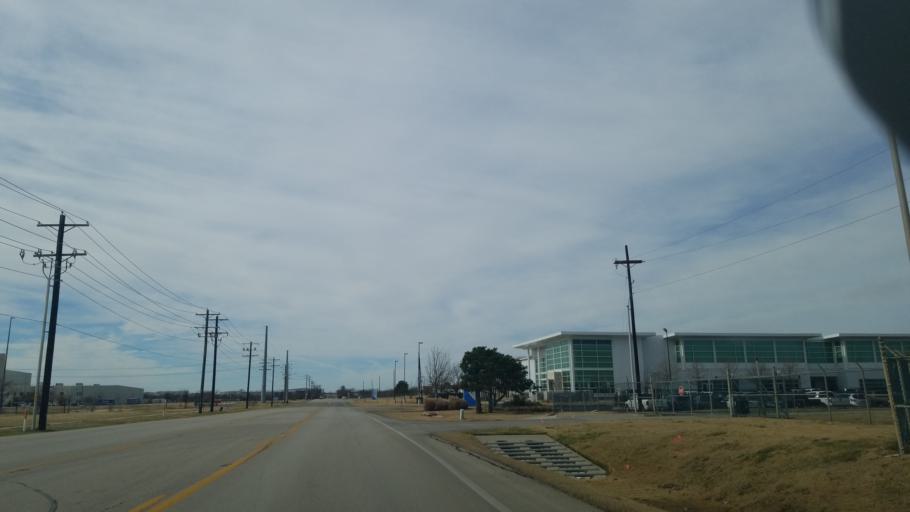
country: US
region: Texas
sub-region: Denton County
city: Denton
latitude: 33.2017
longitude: -97.1788
